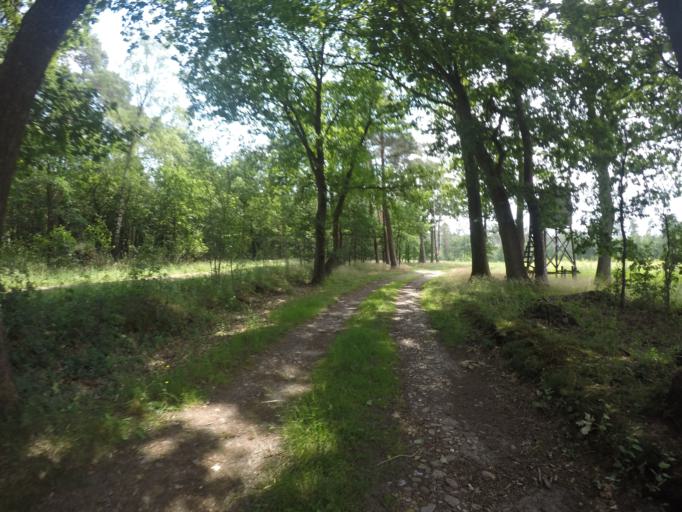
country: DE
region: Lower Saxony
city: Jesteburg
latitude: 53.2693
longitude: 9.9285
